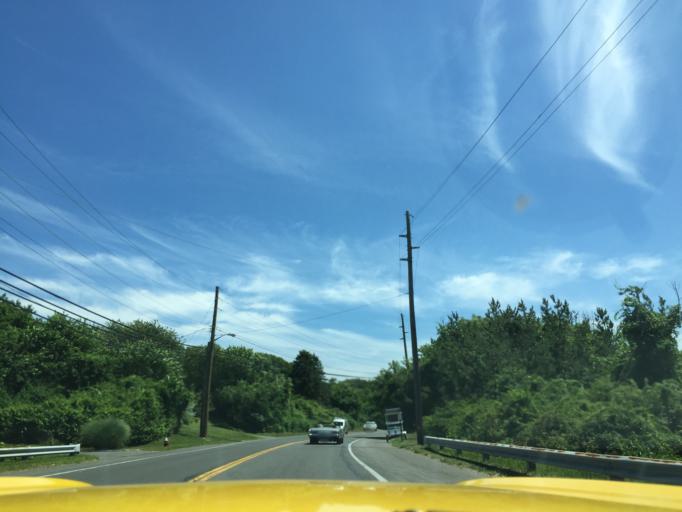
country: US
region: New York
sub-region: Suffolk County
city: Montauk
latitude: 41.0431
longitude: -71.9480
